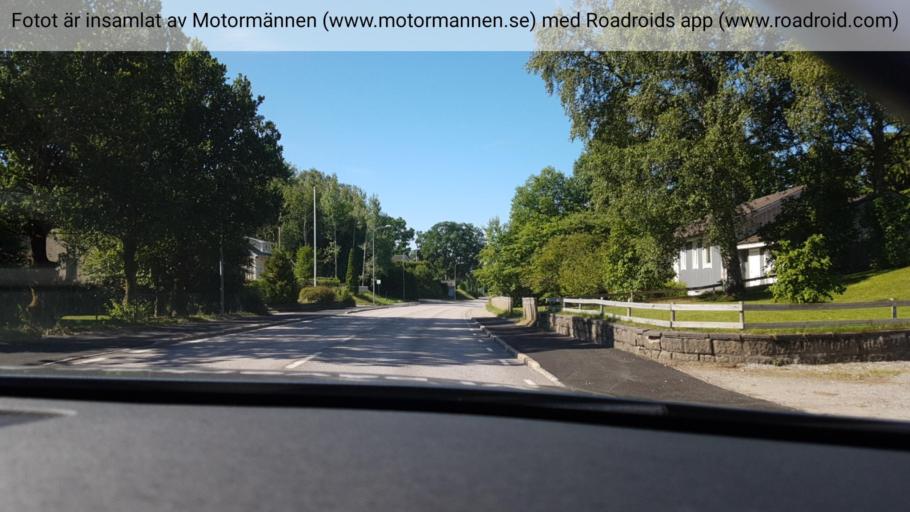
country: SE
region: Vaestra Goetaland
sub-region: Ulricehamns Kommun
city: Ulricehamn
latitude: 57.9022
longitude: 13.4709
